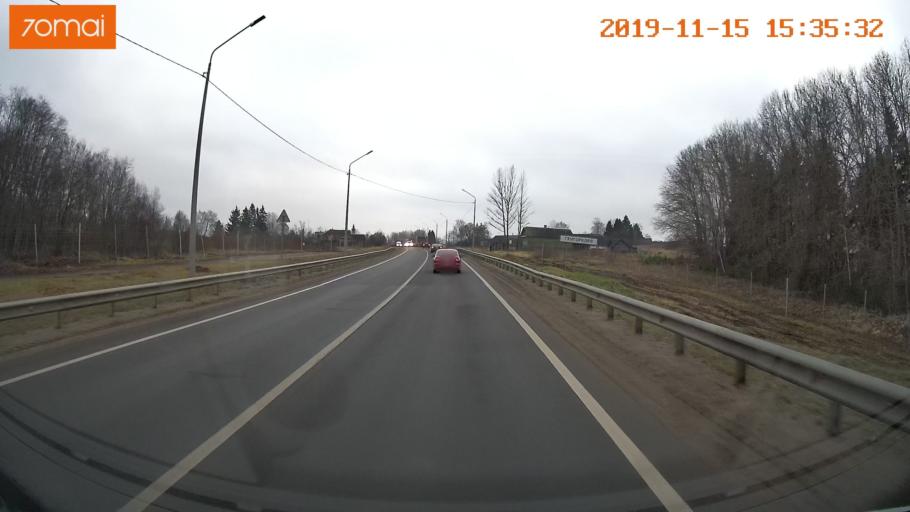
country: RU
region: Jaroslavl
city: Danilov
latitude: 58.0580
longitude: 40.0873
